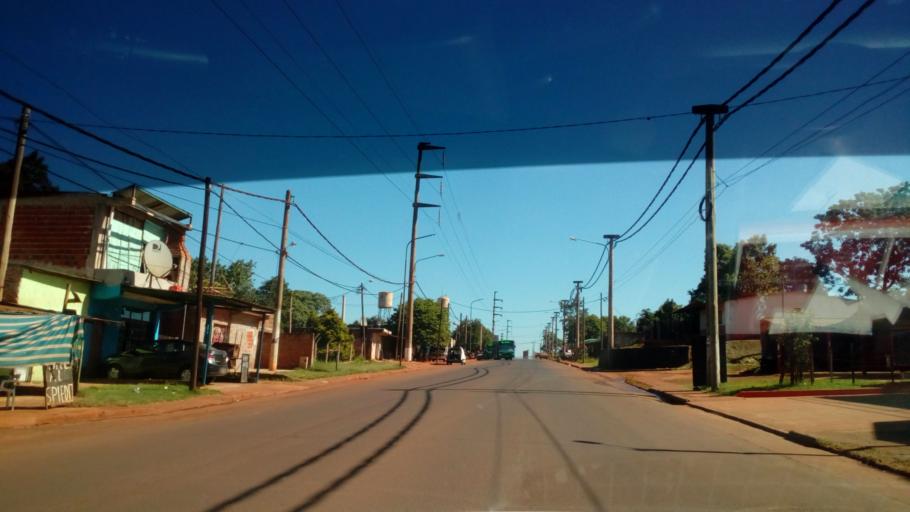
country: AR
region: Misiones
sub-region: Departamento de Capital
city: Posadas
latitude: -27.4249
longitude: -55.9140
